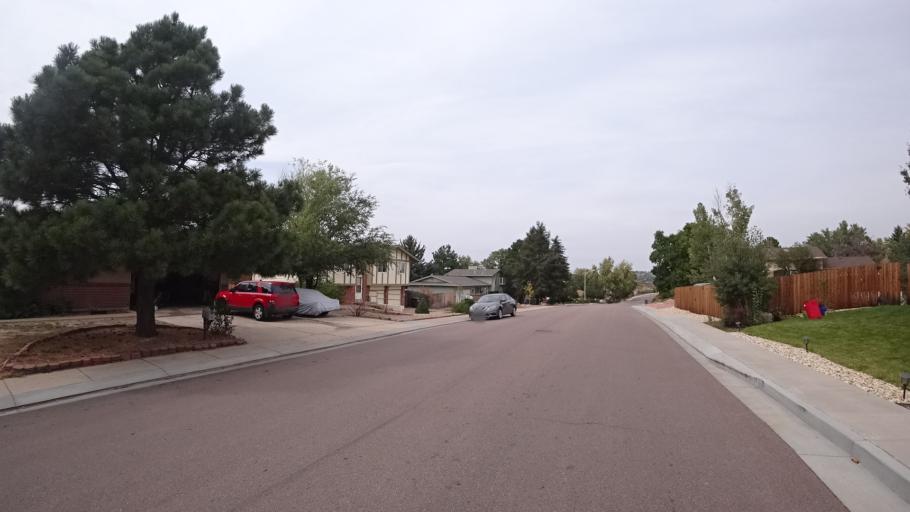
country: US
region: Colorado
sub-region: El Paso County
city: Cimarron Hills
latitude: 38.8928
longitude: -104.7338
